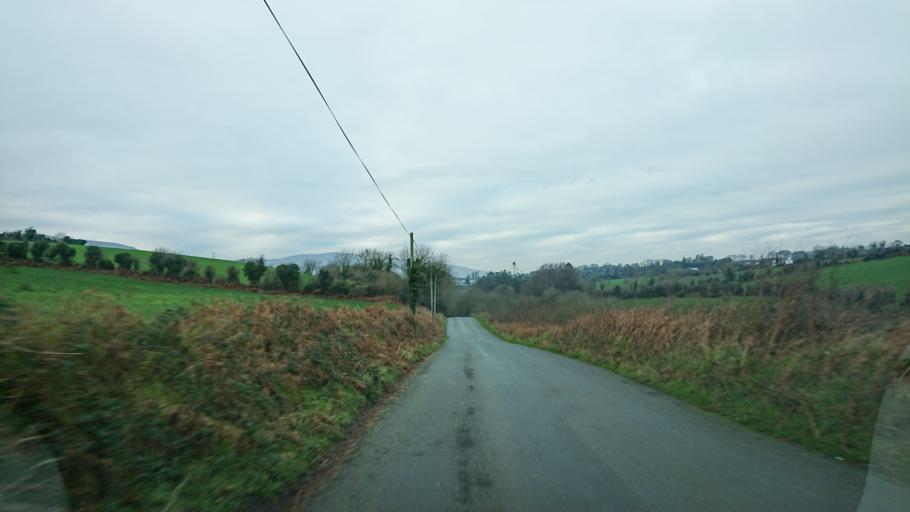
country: IE
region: Munster
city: Carrick-on-Suir
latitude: 52.2781
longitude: -7.4310
